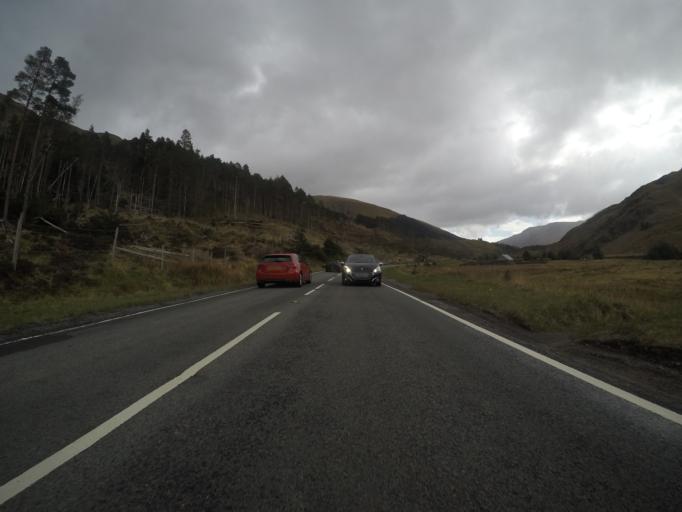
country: GB
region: Scotland
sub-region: Highland
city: Fort William
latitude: 57.1680
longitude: -5.2886
